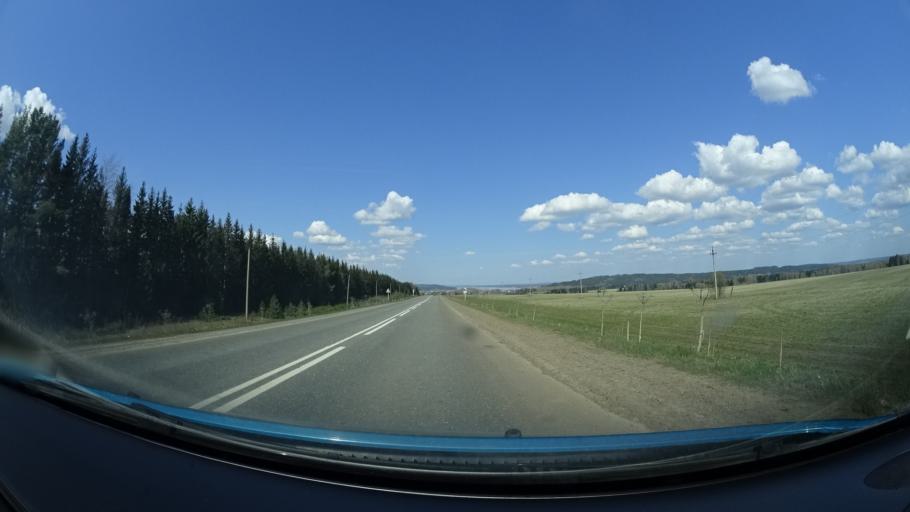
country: RU
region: Perm
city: Osa
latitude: 57.2700
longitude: 55.5712
